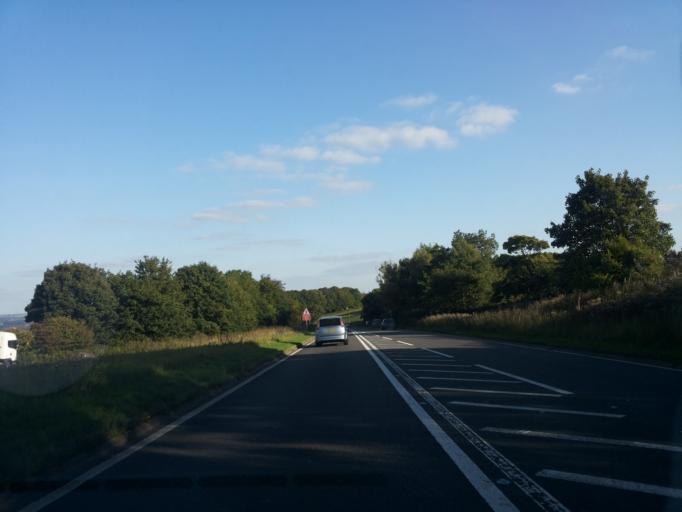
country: GB
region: England
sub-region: Derbyshire
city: Wingerworth
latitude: 53.2311
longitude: -1.5143
